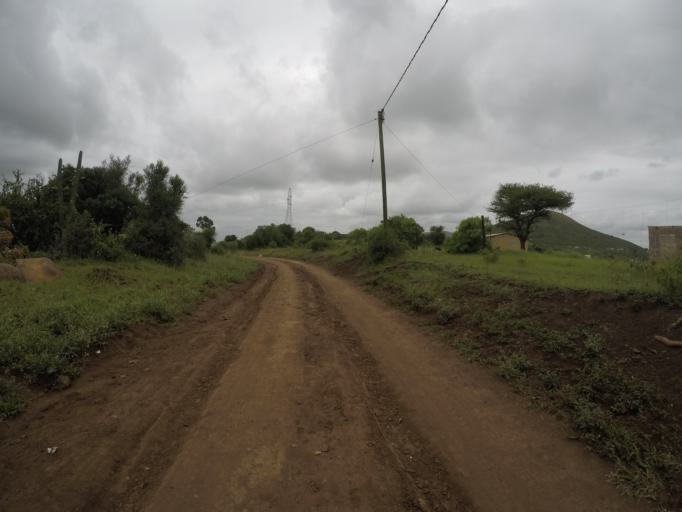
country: ZA
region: KwaZulu-Natal
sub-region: uThungulu District Municipality
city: Empangeni
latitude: -28.6015
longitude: 31.8465
